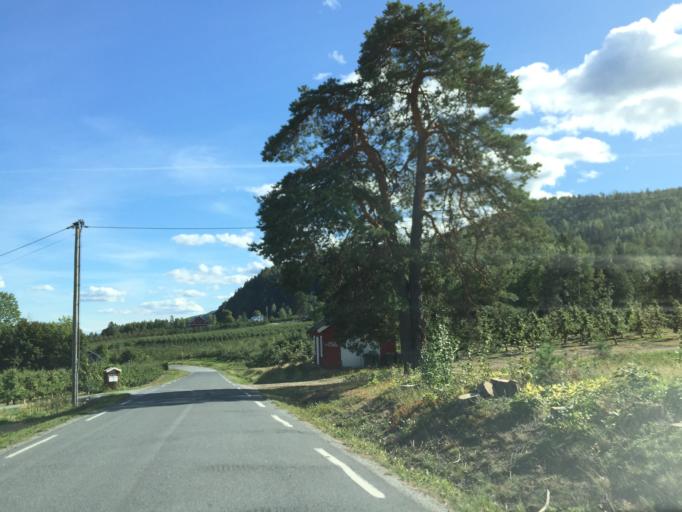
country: NO
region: Buskerud
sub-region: Ovre Eiker
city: Hokksund
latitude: 59.6885
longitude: 9.8487
